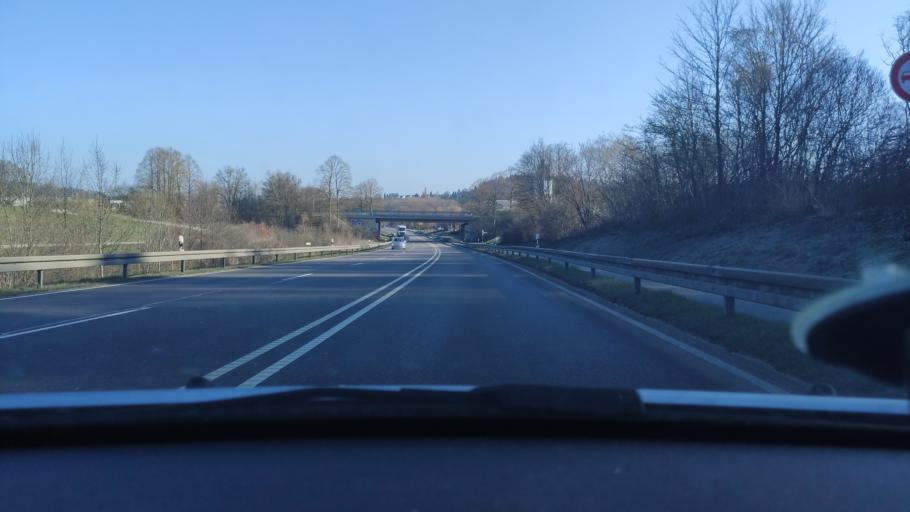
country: DE
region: Baden-Wuerttemberg
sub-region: Tuebingen Region
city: Balingen
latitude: 48.2506
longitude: 8.8546
